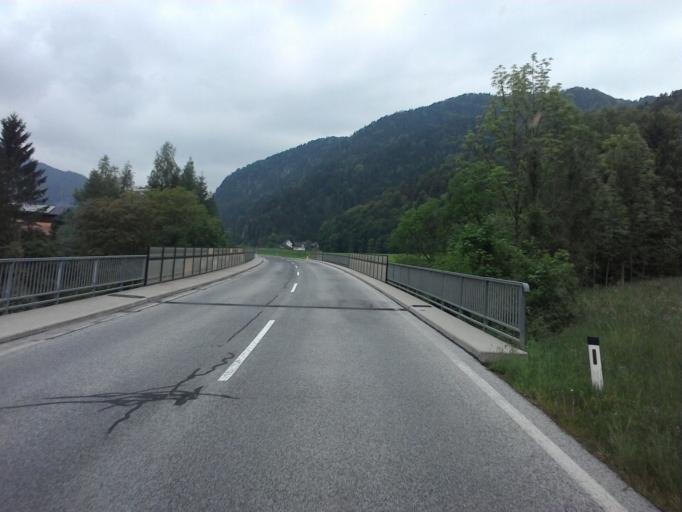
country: AT
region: Styria
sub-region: Politischer Bezirk Liezen
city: Landl
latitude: 47.6859
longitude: 14.7062
